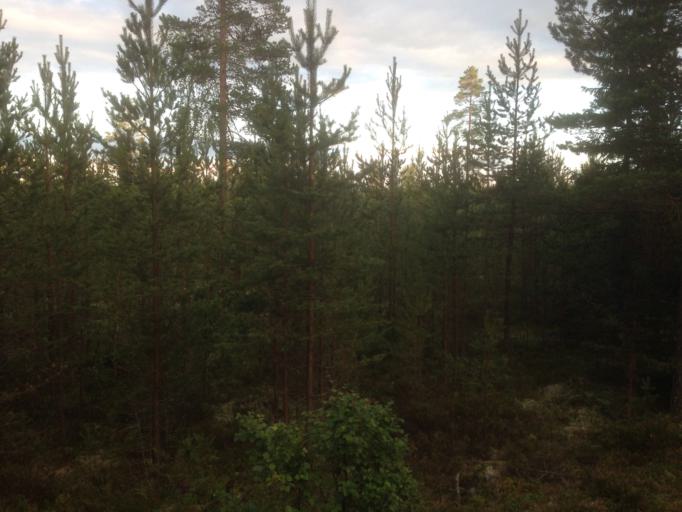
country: SE
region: Dalarna
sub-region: Orsa Kommun
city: Orsa
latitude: 61.2271
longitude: 14.7935
